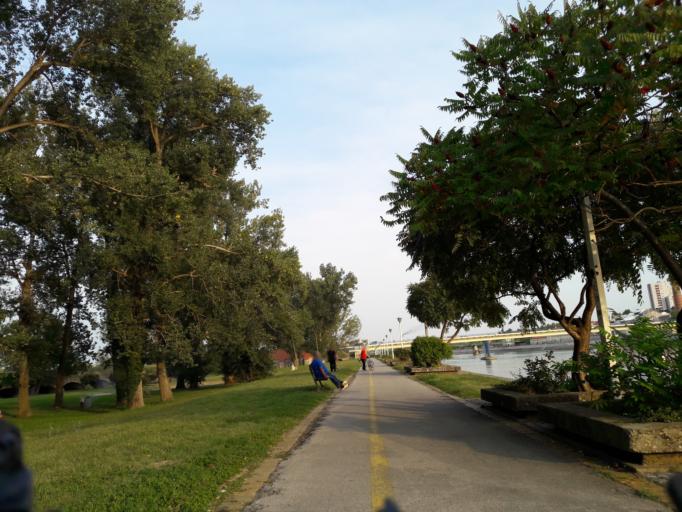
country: HR
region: Osjecko-Baranjska
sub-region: Grad Osijek
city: Osijek
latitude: 45.5643
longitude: 18.6986
